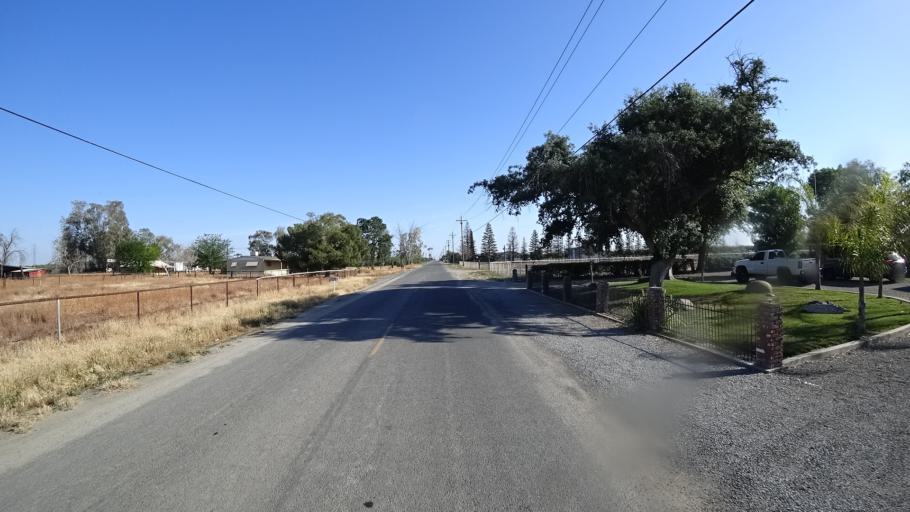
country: US
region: California
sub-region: Kings County
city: Corcoran
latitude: 36.1112
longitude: -119.5542
